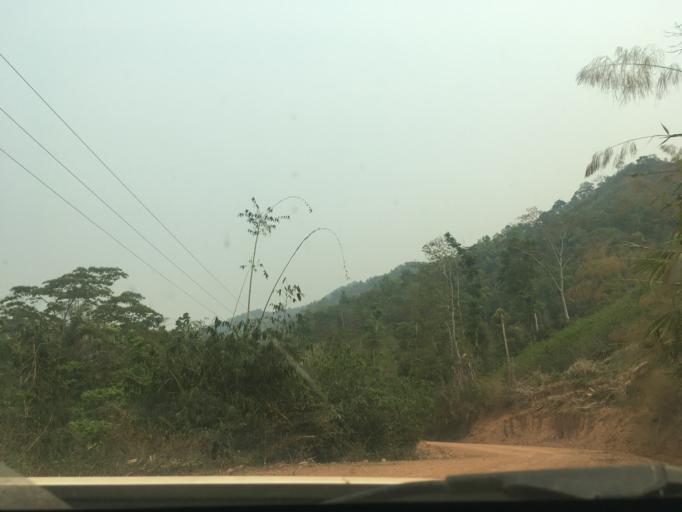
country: VN
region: Huyen Dien Bien
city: Thi Tran Muong Cha
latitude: 21.7321
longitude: 102.8379
